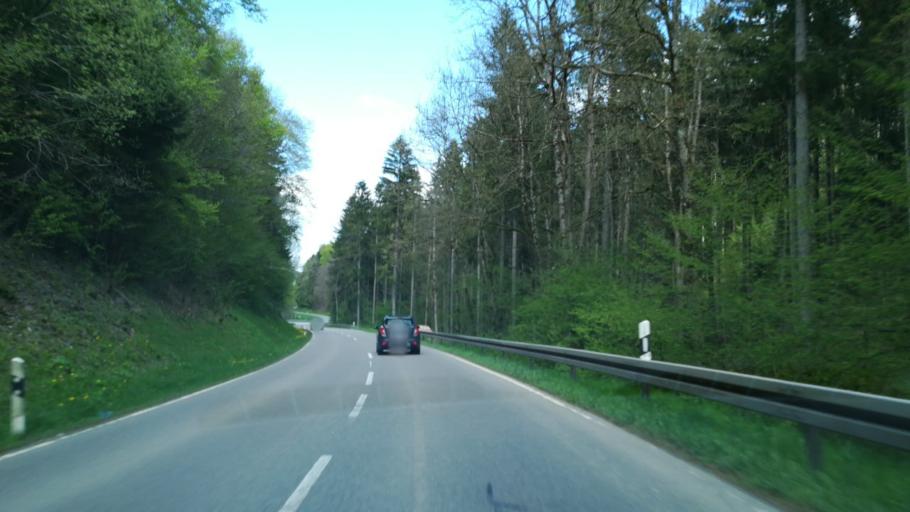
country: DE
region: Baden-Wuerttemberg
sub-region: Freiburg Region
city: Bonndorf im Schwarzwald
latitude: 47.8314
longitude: 8.4246
